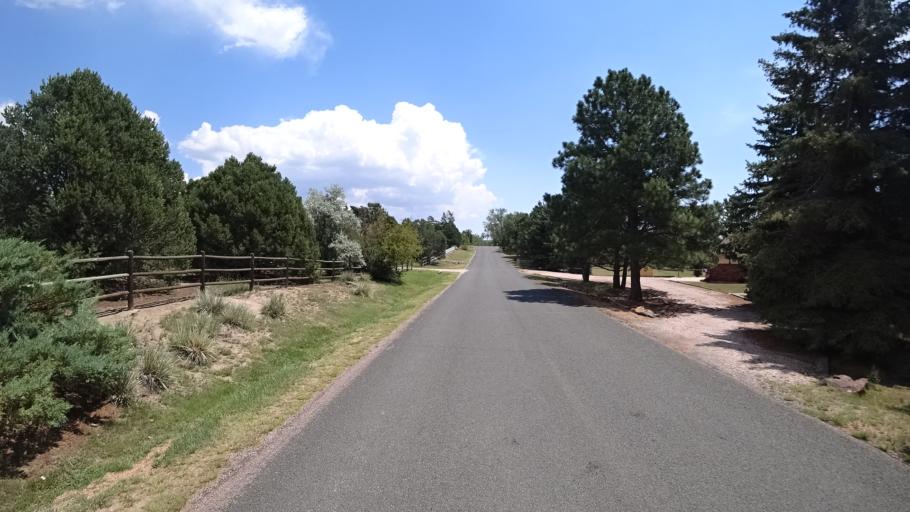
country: US
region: Colorado
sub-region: El Paso County
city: Air Force Academy
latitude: 38.9396
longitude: -104.8047
